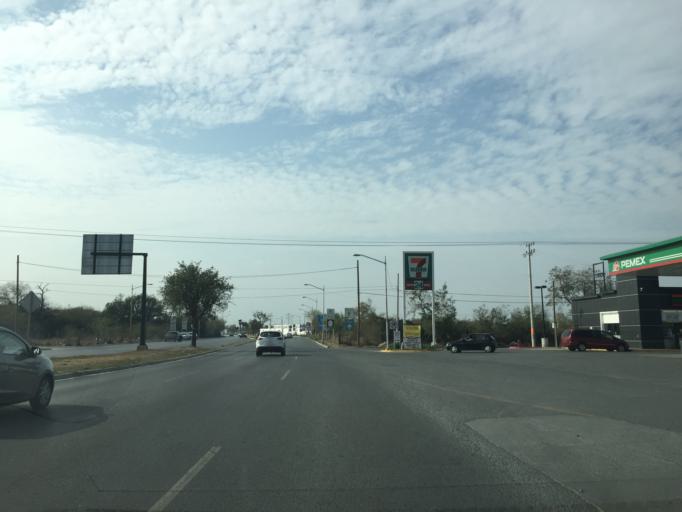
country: MX
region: Nuevo Leon
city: Apodaca
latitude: 25.7730
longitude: -100.2010
